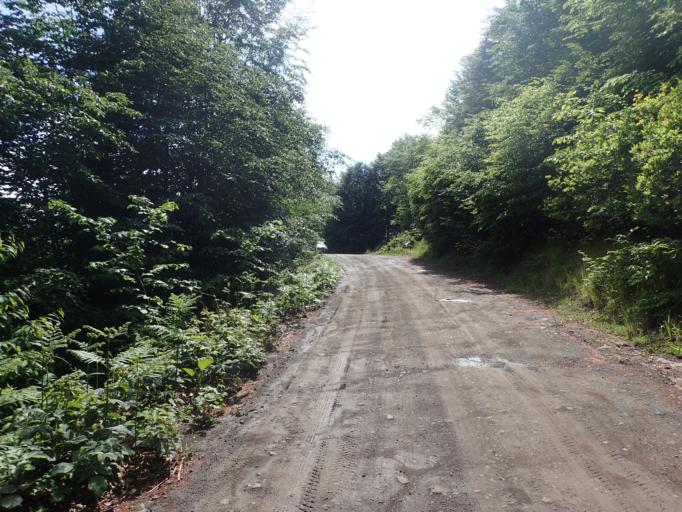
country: TR
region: Samsun
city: Salipazari
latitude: 40.9414
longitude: 36.8708
